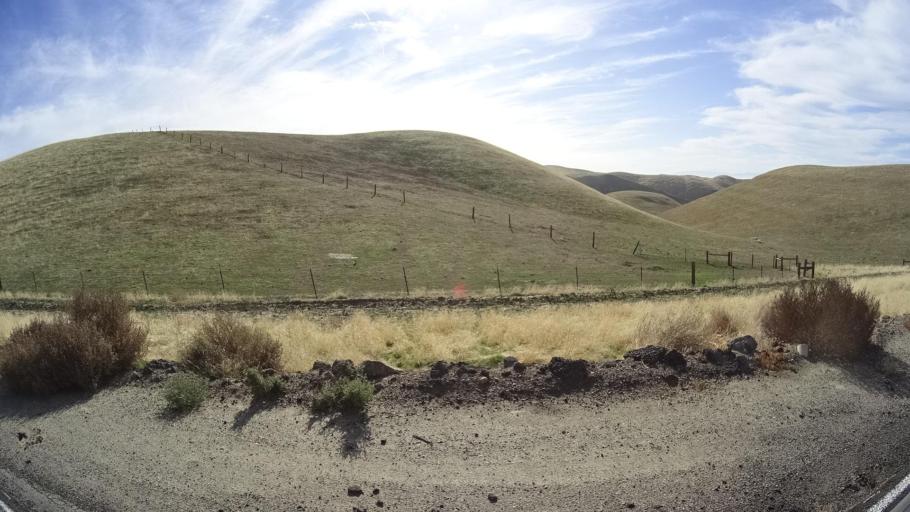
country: US
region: California
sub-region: Kern County
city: Oildale
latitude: 35.6091
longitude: -118.8943
